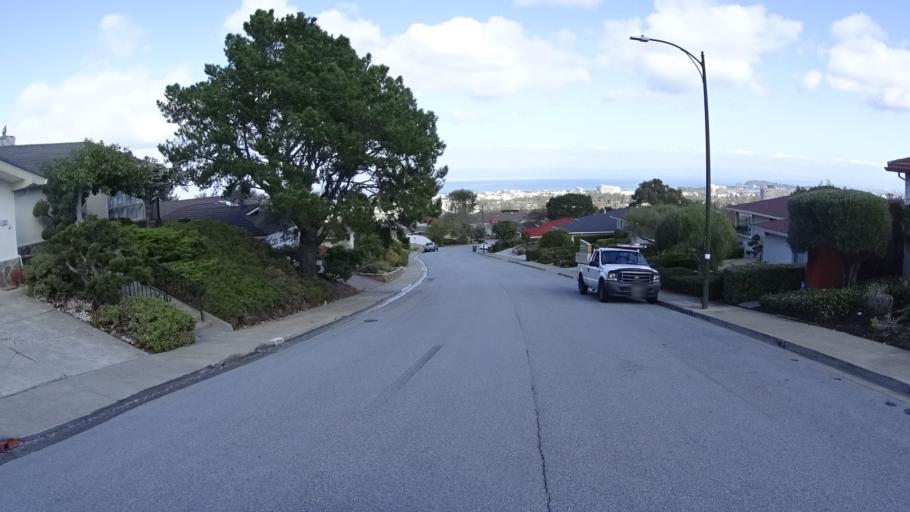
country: US
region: California
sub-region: San Mateo County
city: Millbrae
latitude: 37.5847
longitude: -122.3953
